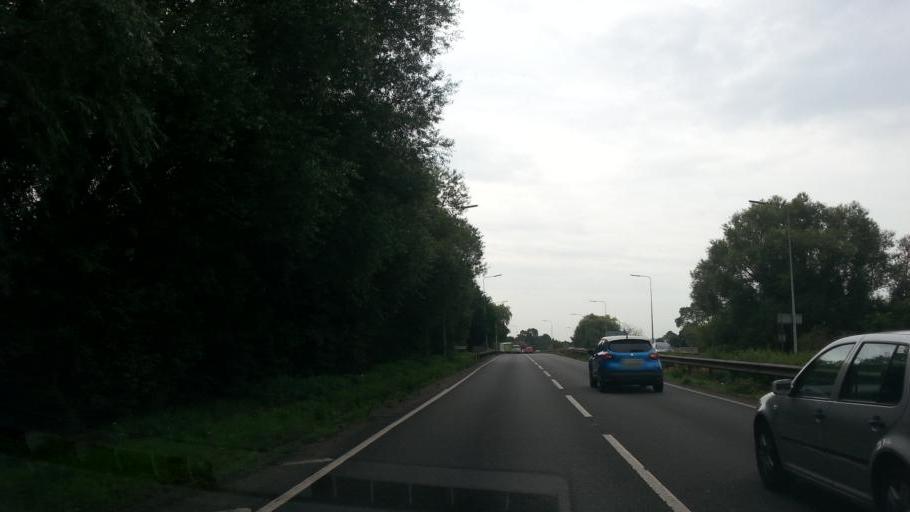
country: GB
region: England
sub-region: Central Bedfordshire
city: Sandy
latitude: 52.1260
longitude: -0.2986
